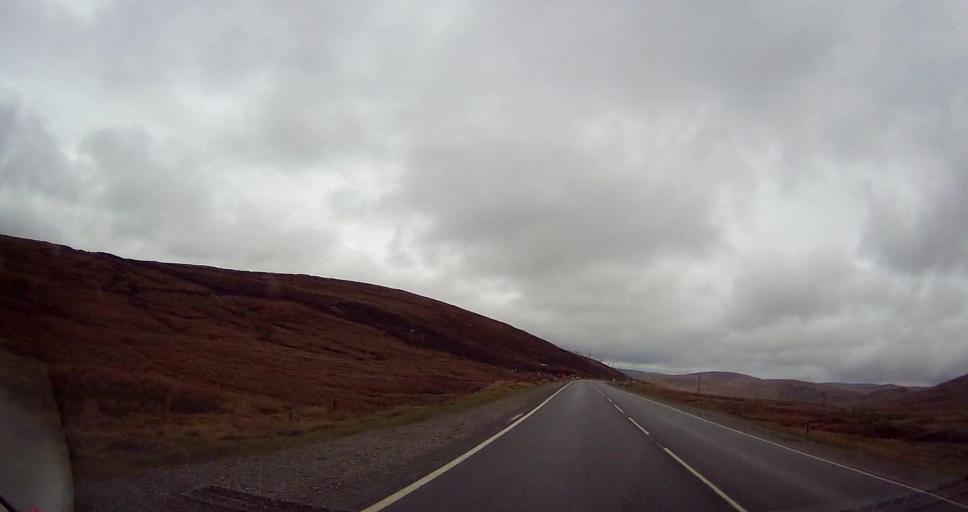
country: GB
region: Scotland
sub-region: Shetland Islands
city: Lerwick
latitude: 60.3277
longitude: -1.2530
